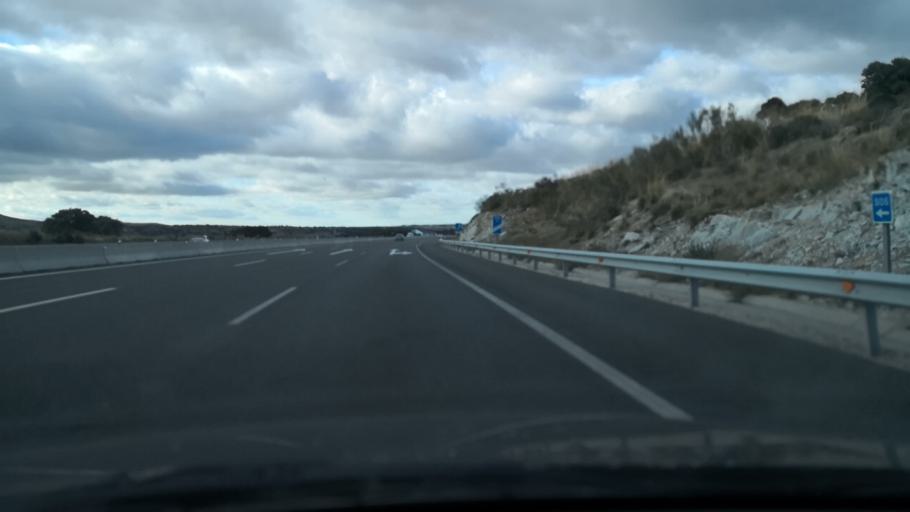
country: ES
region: Castille and Leon
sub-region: Provincia de Segovia
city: Zarzuela del Monte
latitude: 40.7449
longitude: -4.3344
